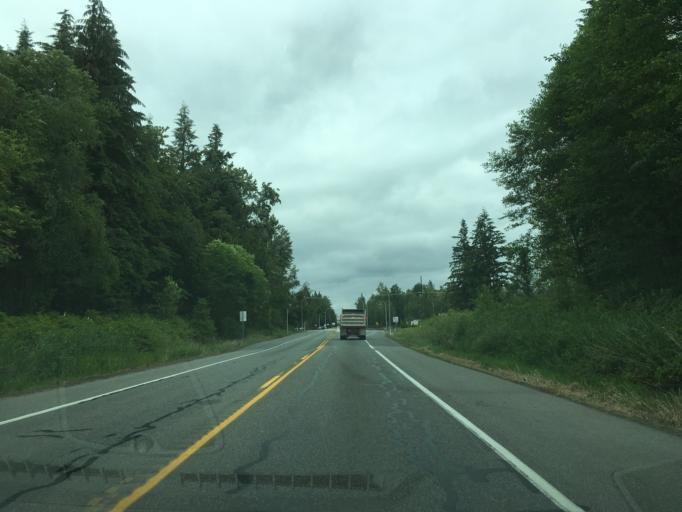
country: US
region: Washington
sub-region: Snohomish County
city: Sisco Heights
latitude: 48.0693
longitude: -122.1112
